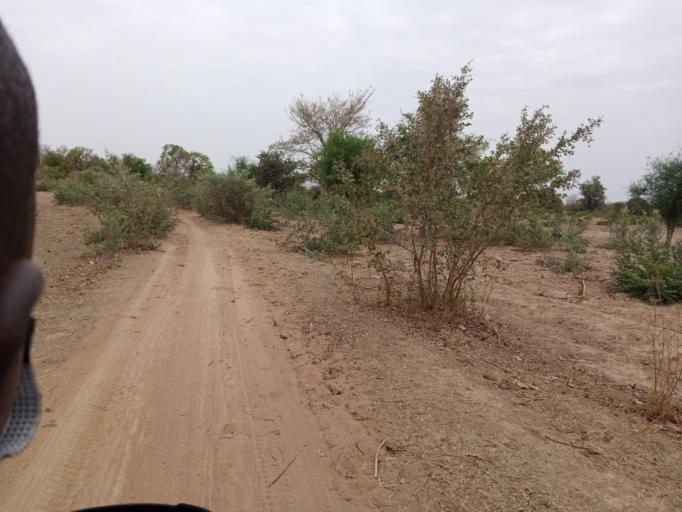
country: BF
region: Boucle du Mouhoun
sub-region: Province de la Kossi
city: Nouna
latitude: 12.8310
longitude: -4.0770
